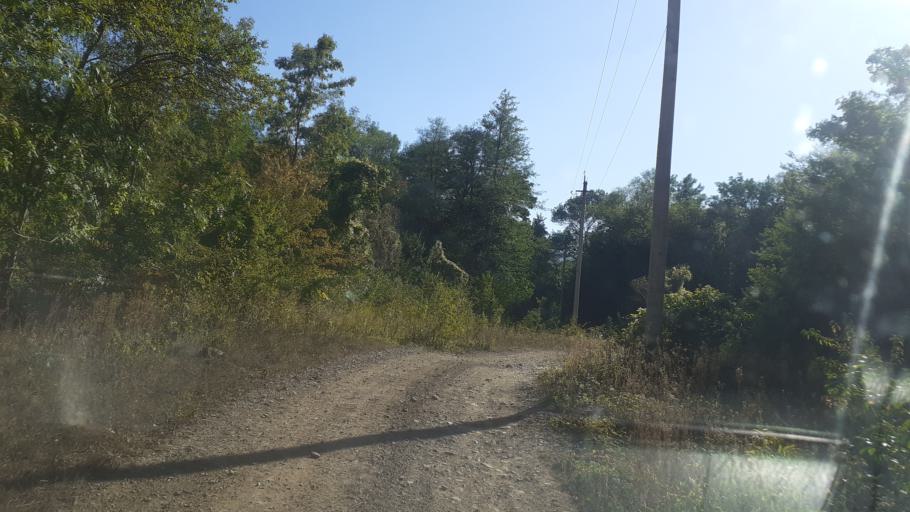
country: RU
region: Krasnodarskiy
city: Azovskaya
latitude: 44.7177
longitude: 38.5299
